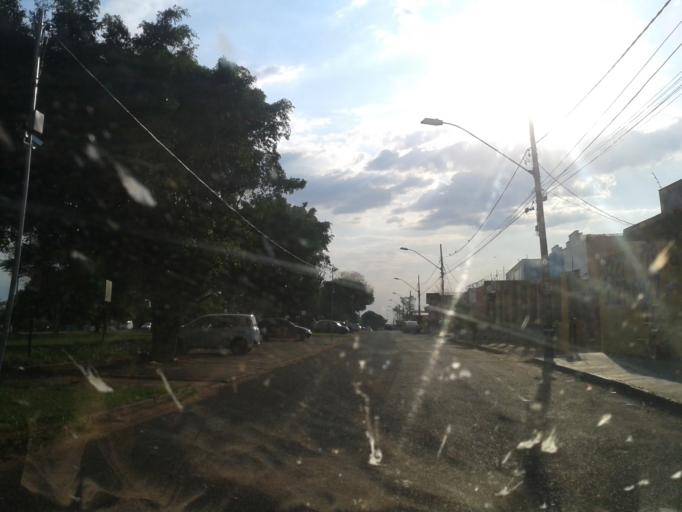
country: BR
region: Minas Gerais
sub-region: Uberlandia
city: Uberlandia
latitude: -18.9397
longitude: -48.3110
